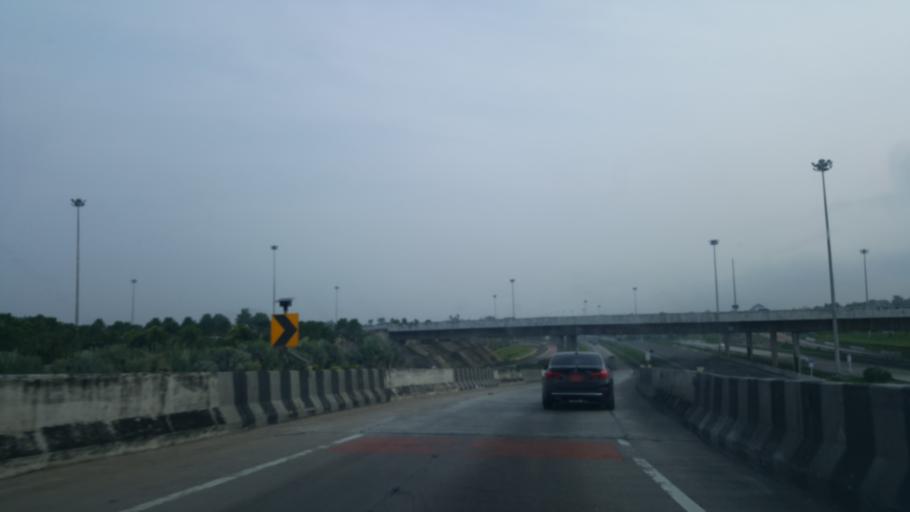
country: TH
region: Chon Buri
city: Bang Lamung
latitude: 12.9644
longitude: 100.9789
